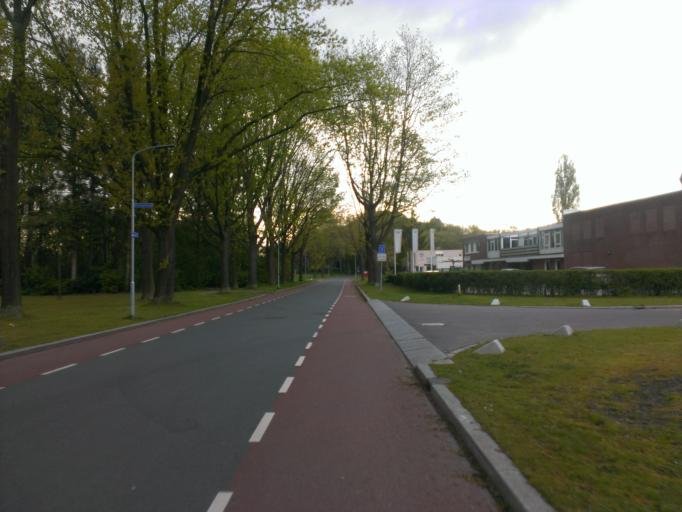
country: NL
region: Gelderland
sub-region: Gemeente Heerde
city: Heerde
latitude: 52.3953
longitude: 6.0430
